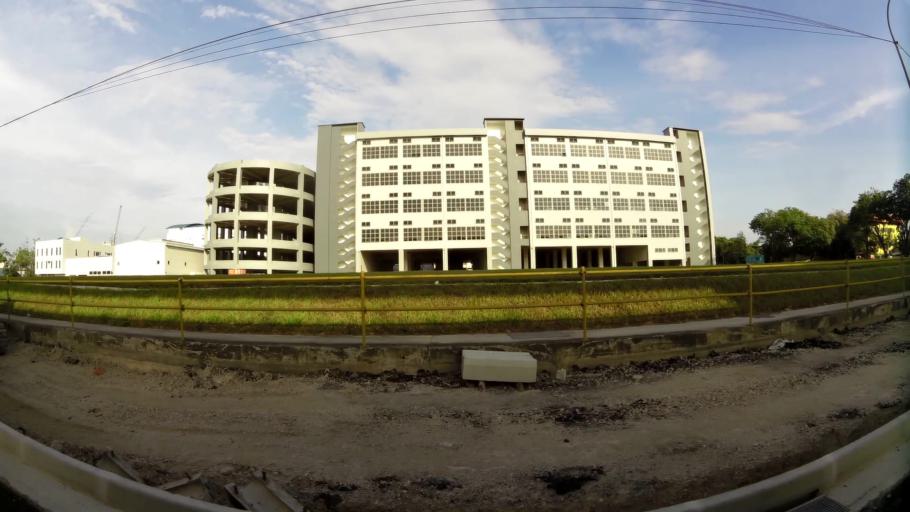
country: MY
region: Johor
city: Johor Bahru
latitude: 1.3180
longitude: 103.6588
